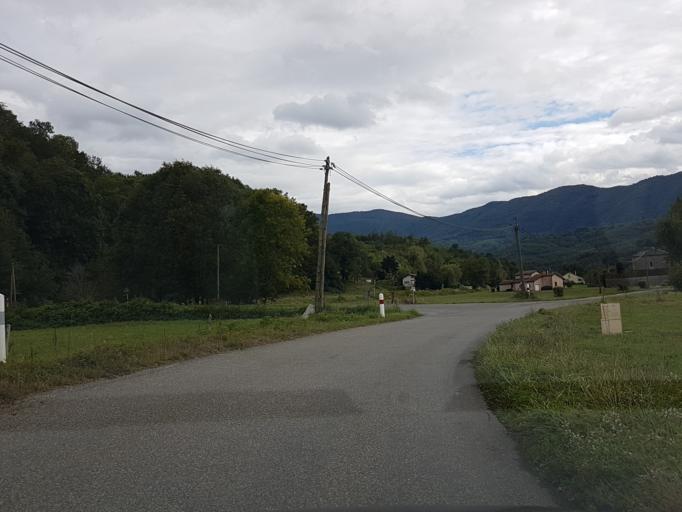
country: FR
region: Midi-Pyrenees
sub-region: Departement de l'Ariege
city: Saint-Girons
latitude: 42.8877
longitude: 1.2139
